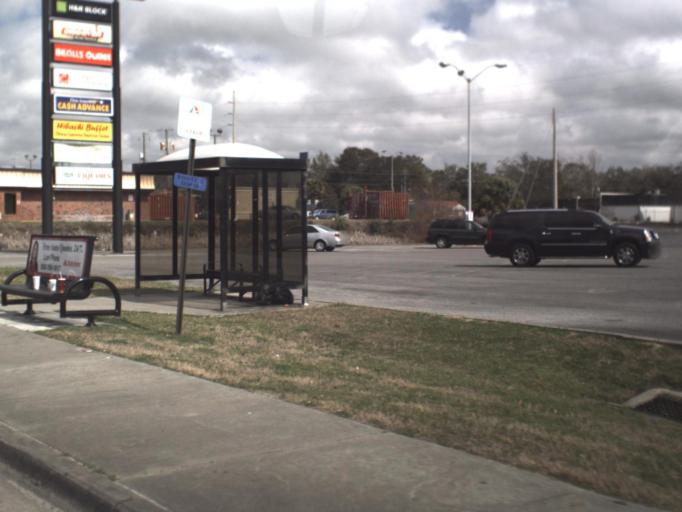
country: US
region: Florida
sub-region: Bay County
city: Parker
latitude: 30.1441
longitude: -85.5911
